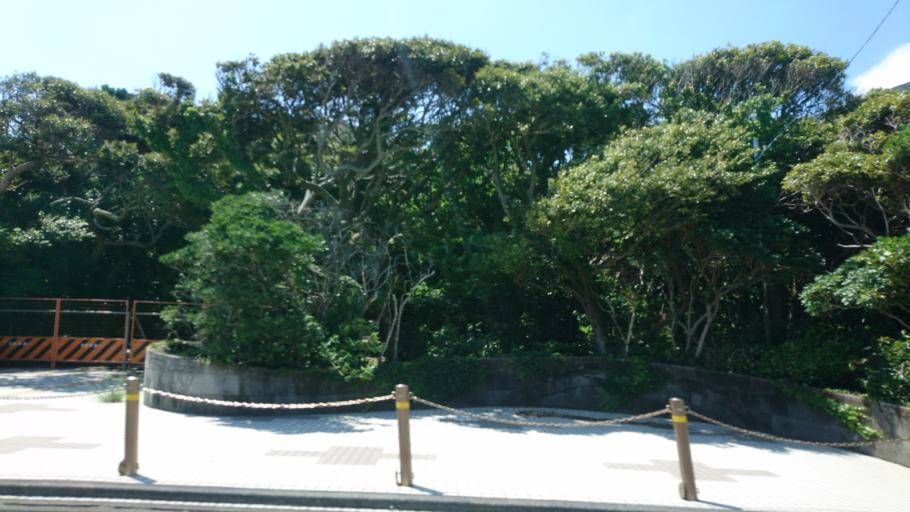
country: JP
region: Shizuoka
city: Shimoda
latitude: 34.3786
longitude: 139.2719
